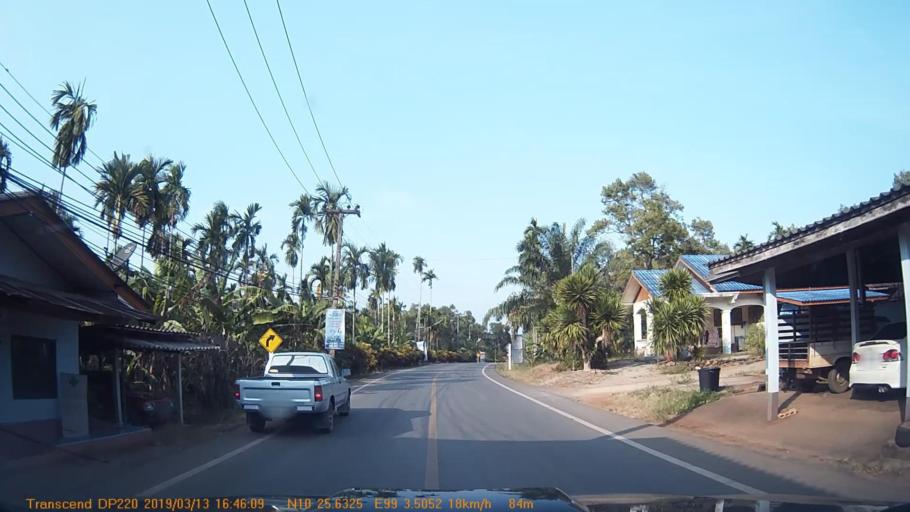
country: TH
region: Chumphon
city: Chumphon
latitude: 10.4271
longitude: 99.0584
